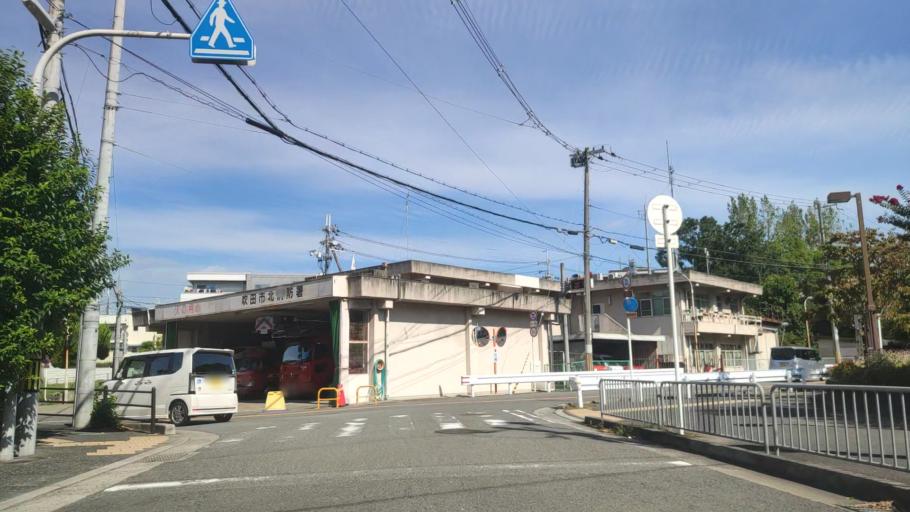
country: JP
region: Osaka
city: Mino
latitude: 34.8113
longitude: 135.5167
